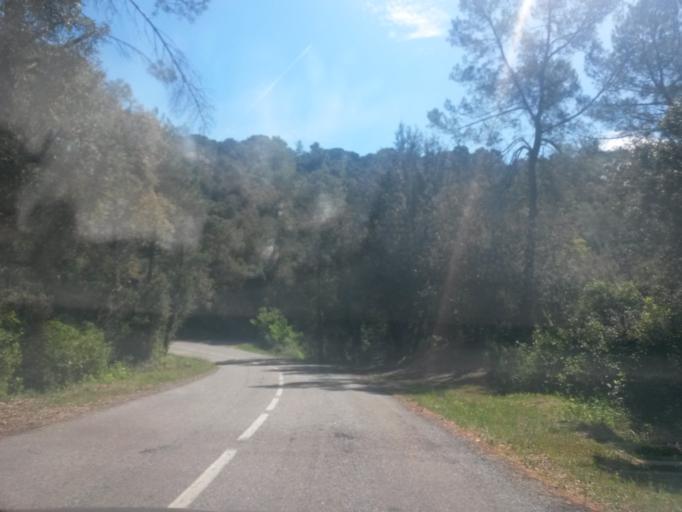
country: ES
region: Catalonia
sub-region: Provincia de Girona
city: Madremanya
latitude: 41.9834
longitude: 2.9466
